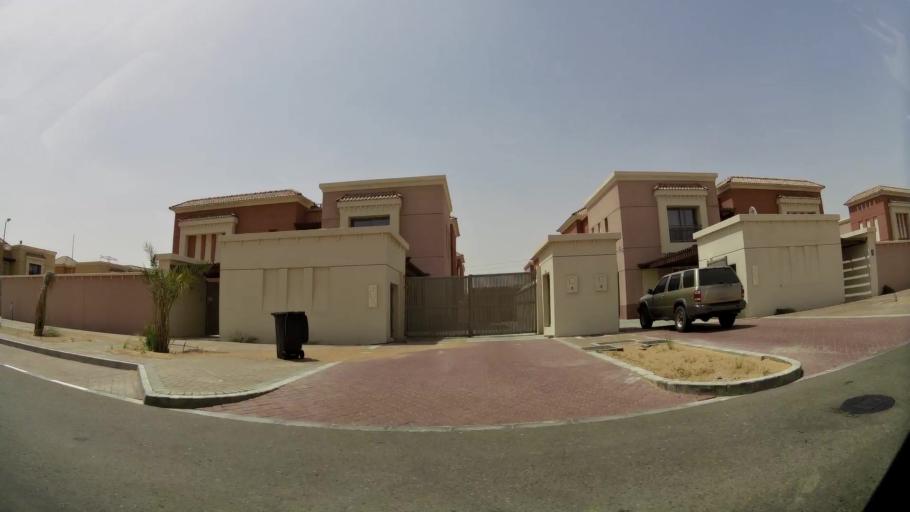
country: AE
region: Abu Dhabi
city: Al Ain
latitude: 24.1485
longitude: 55.6302
